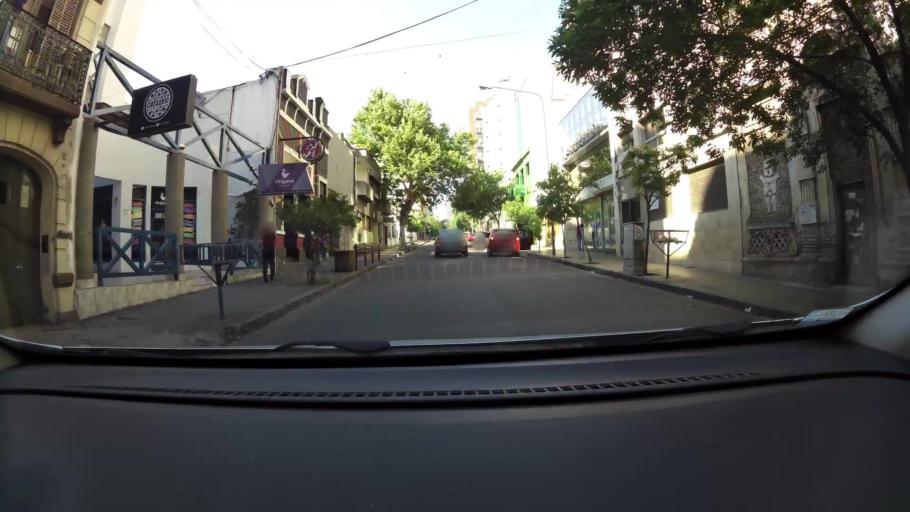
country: AR
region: Cordoba
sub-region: Departamento de Capital
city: Cordoba
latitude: -31.4220
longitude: -64.1835
